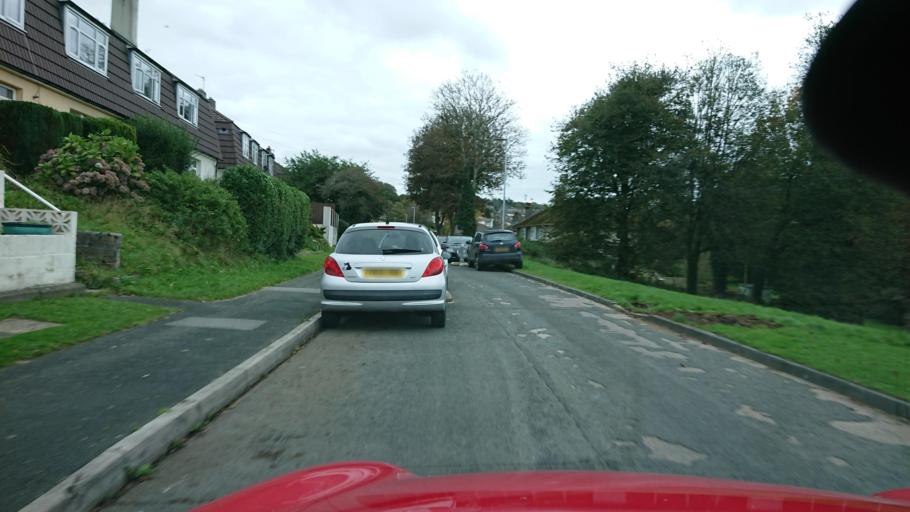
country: GB
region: England
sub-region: Plymouth
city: Plymouth
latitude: 50.4148
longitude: -4.1473
